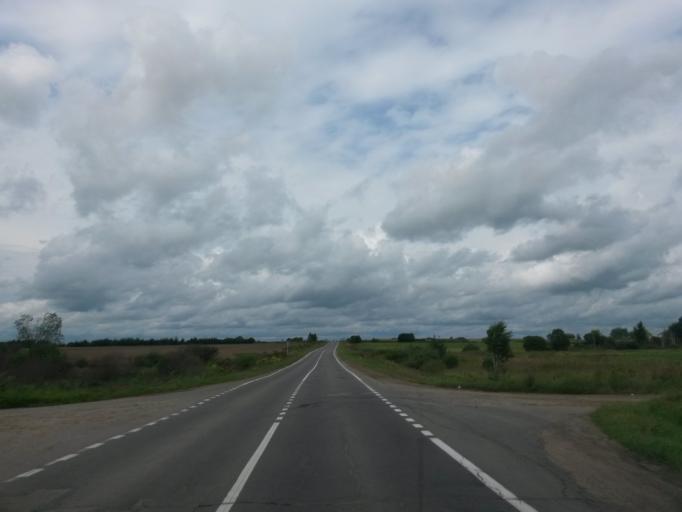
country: RU
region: Jaroslavl
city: Yaroslavl
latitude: 57.7474
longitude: 39.8817
